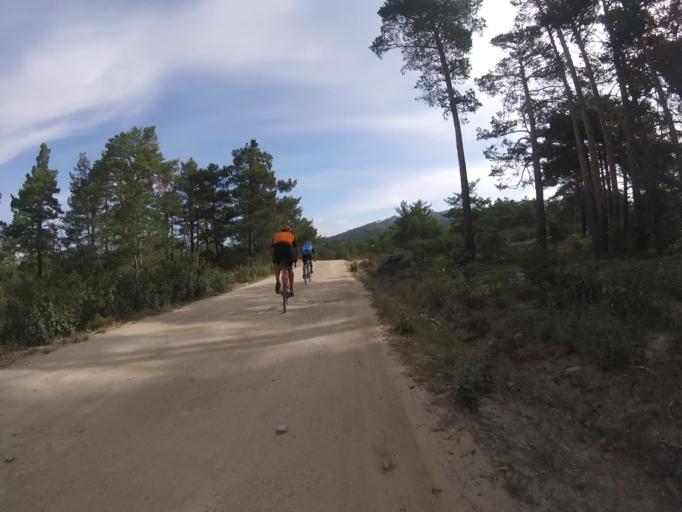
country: ES
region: Castille and Leon
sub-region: Provincia de Avila
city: Peguerinos
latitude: 40.6449
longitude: -4.1786
